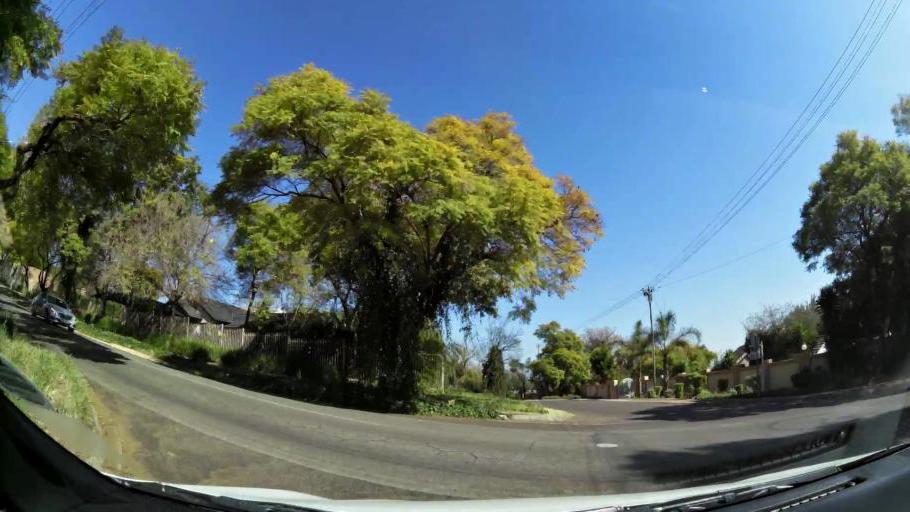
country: ZA
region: Gauteng
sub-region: City of Tshwane Metropolitan Municipality
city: Pretoria
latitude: -25.7976
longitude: 28.2403
